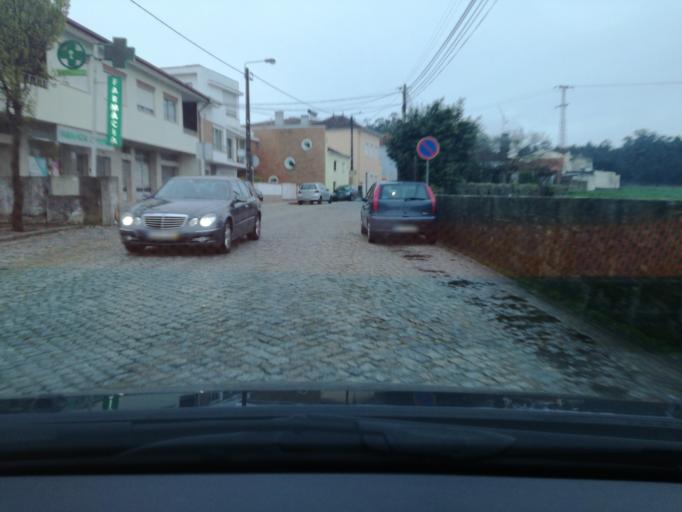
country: PT
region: Porto
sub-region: Maia
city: Gemunde
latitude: 41.2671
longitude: -8.6435
